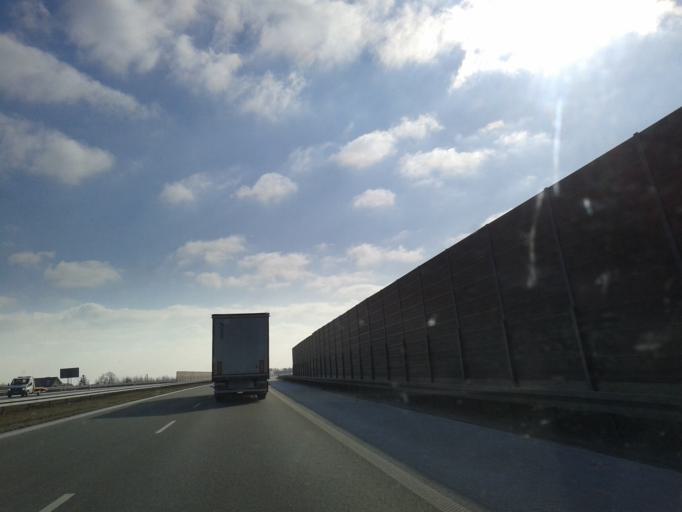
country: PL
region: Kujawsko-Pomorskie
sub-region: Powiat aleksandrowski
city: Waganiec
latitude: 52.7535
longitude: 18.8584
